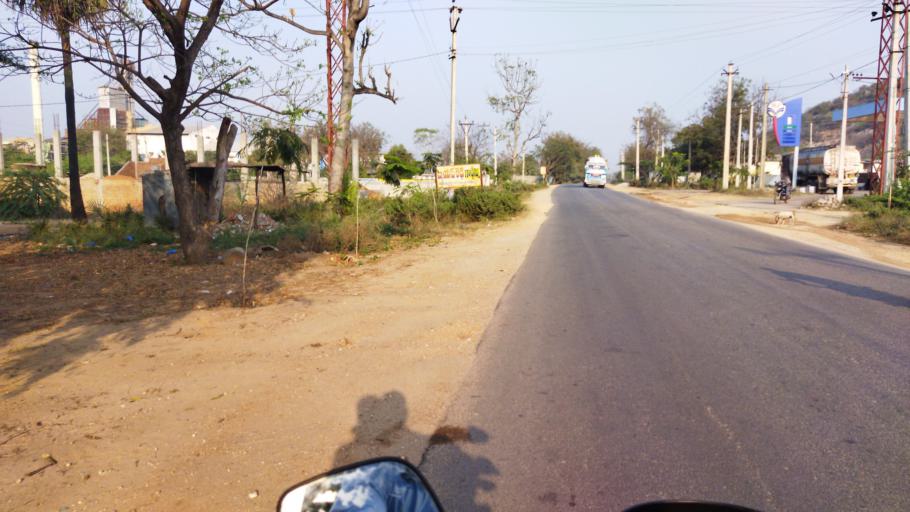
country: IN
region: Telangana
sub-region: Nalgonda
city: Nalgonda
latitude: 17.2383
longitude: 79.1189
